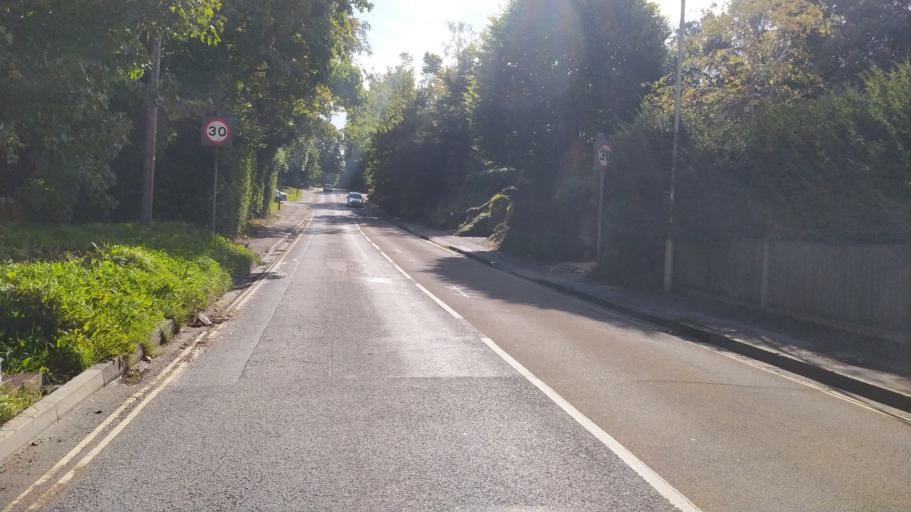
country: GB
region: England
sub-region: Hampshire
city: Winchester
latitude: 51.0750
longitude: -1.3227
